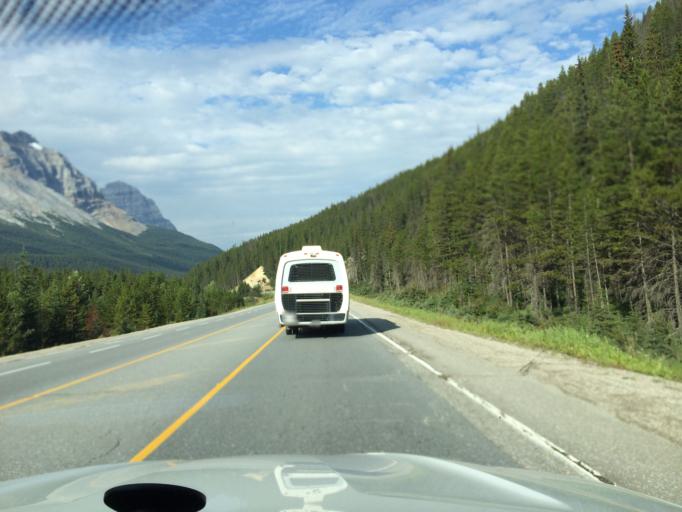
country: CA
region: Alberta
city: Lake Louise
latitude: 51.4476
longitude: -116.3275
